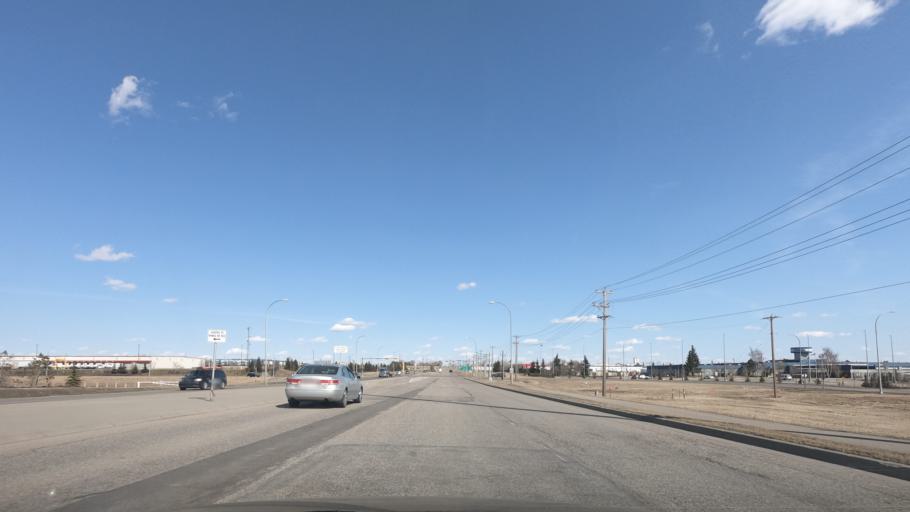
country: CA
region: Alberta
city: Airdrie
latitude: 51.2999
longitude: -113.9975
